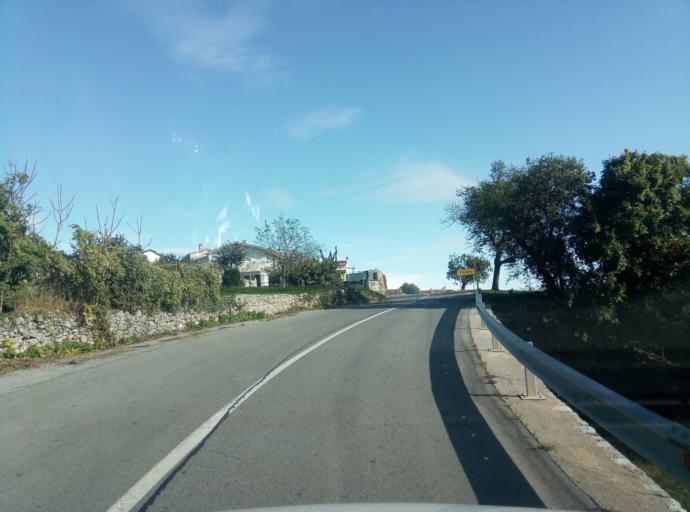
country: SI
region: Komen
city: Komen
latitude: 45.8146
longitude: 13.8070
